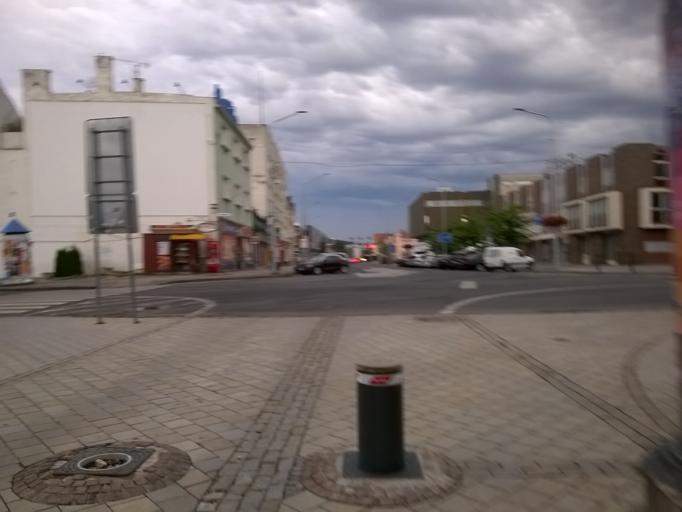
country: SK
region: Nitriansky
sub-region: Okres Nitra
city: Nitra
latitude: 48.3102
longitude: 18.0865
